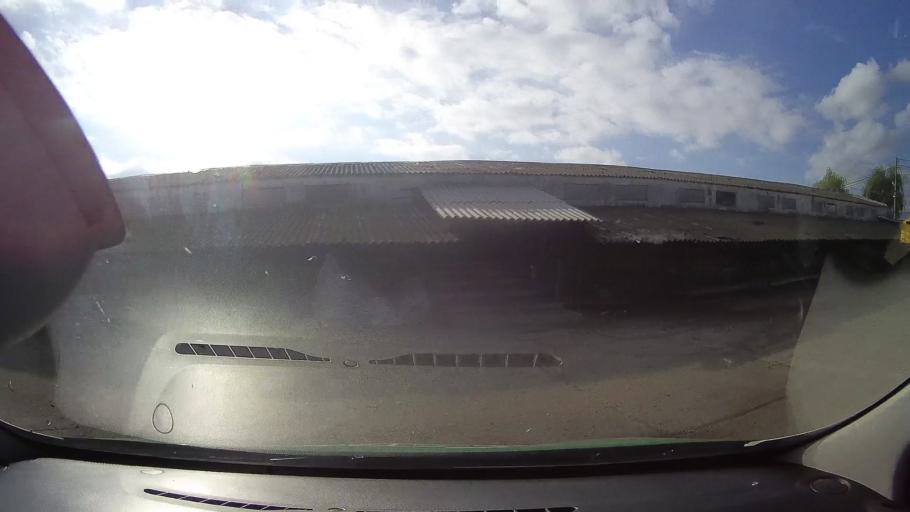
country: RO
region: Constanta
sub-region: Comuna Sacele
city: Sacele
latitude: 44.4802
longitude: 28.6509
